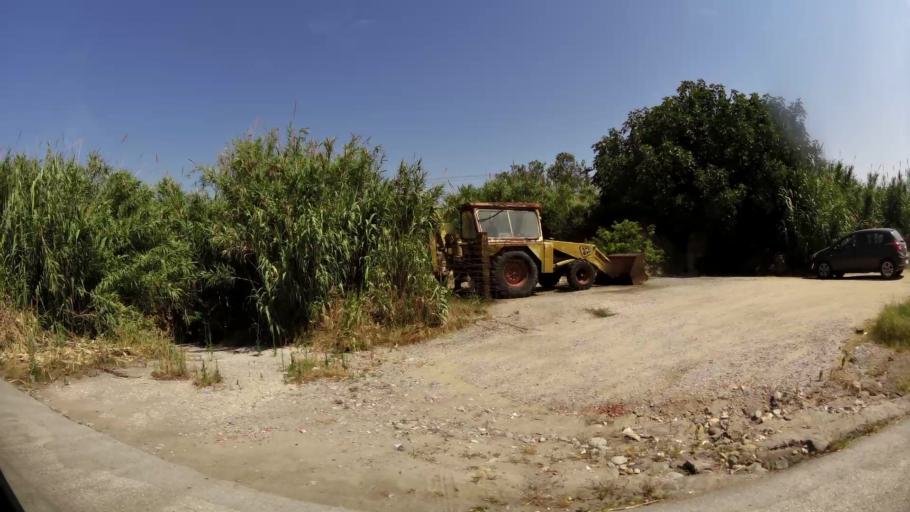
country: GR
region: Central Macedonia
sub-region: Nomos Thessalonikis
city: Neoi Epivates
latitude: 40.5001
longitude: 22.9081
